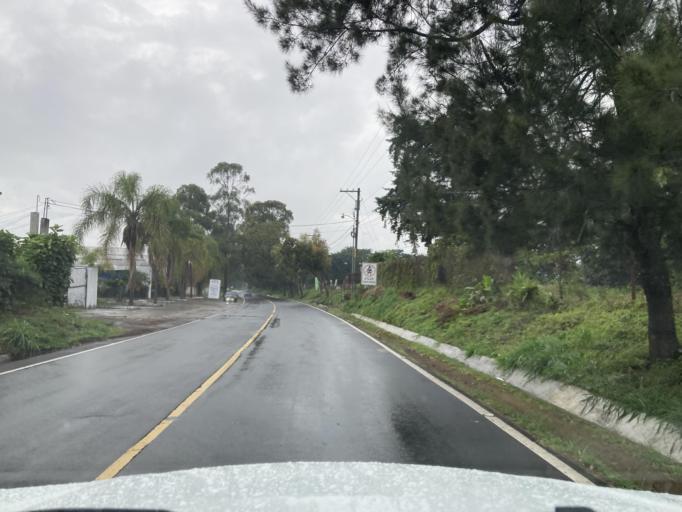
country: GT
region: Sacatepequez
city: San Miguel Duenas
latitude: 14.5197
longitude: -90.7792
